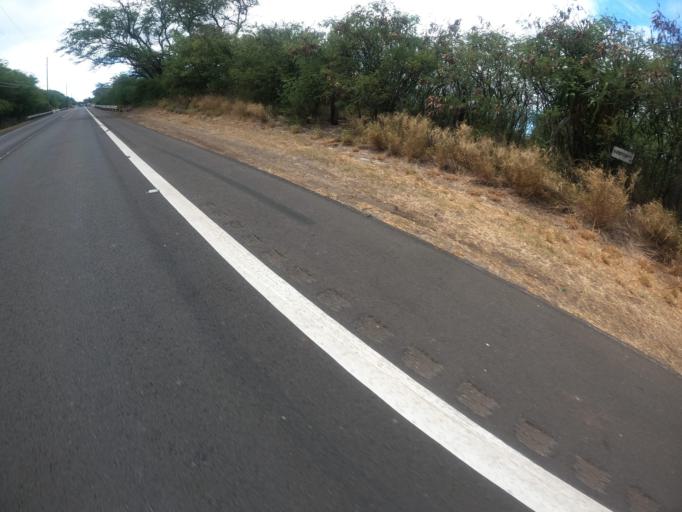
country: US
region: Hawaii
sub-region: Honolulu County
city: Makaha Valley
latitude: 21.5091
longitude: -158.2288
